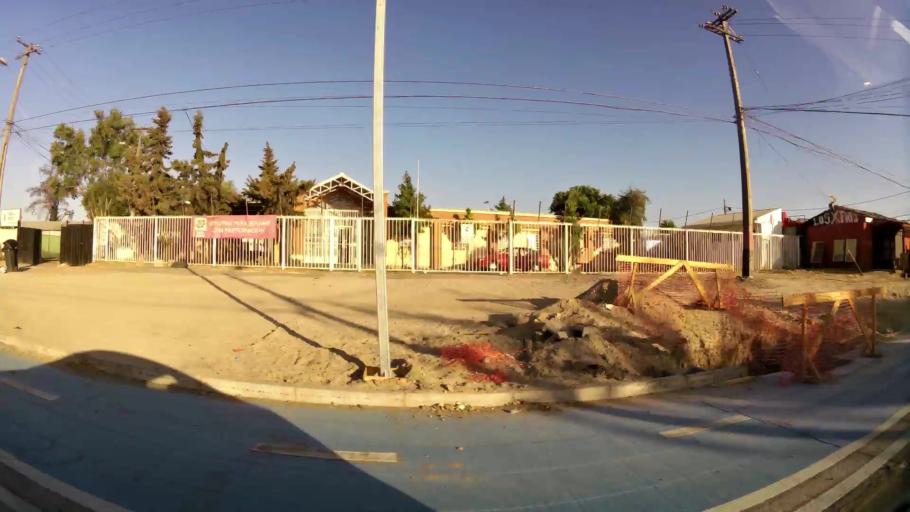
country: CL
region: Maule
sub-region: Provincia de Talca
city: Talca
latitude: -35.4329
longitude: -71.6412
